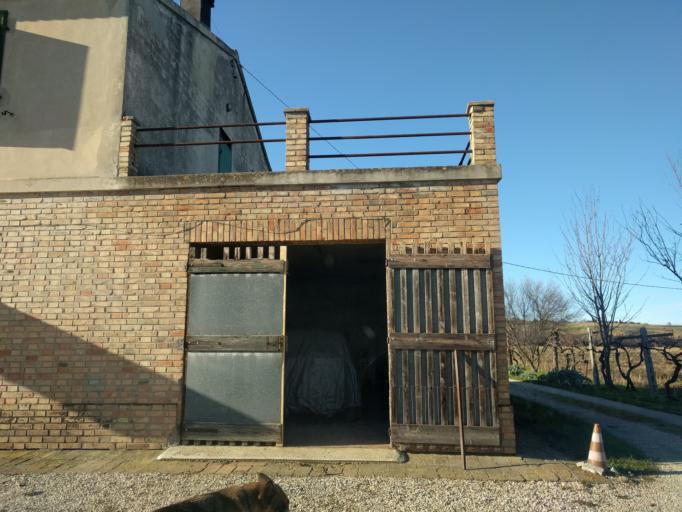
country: IT
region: The Marches
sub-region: Provincia di Pesaro e Urbino
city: Lucrezia
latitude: 43.7809
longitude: 12.9517
